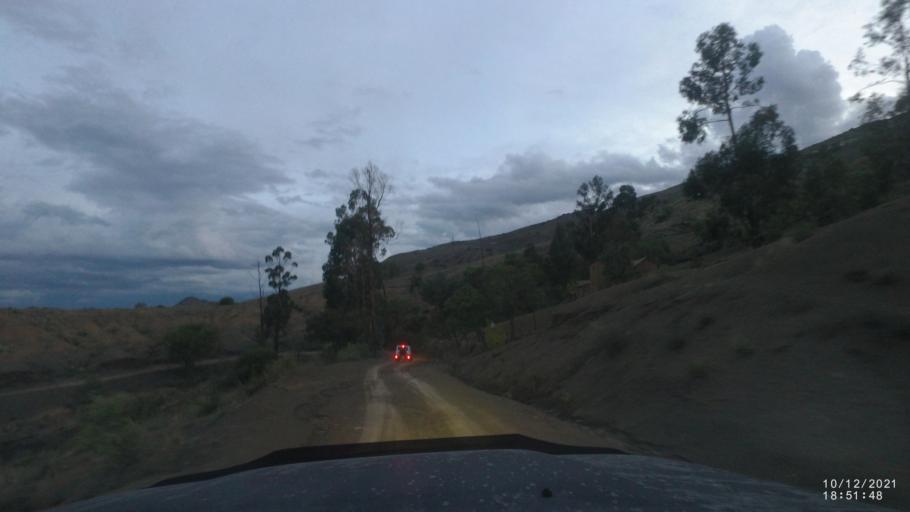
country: BO
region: Cochabamba
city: Tarata
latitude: -17.8830
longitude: -65.9646
